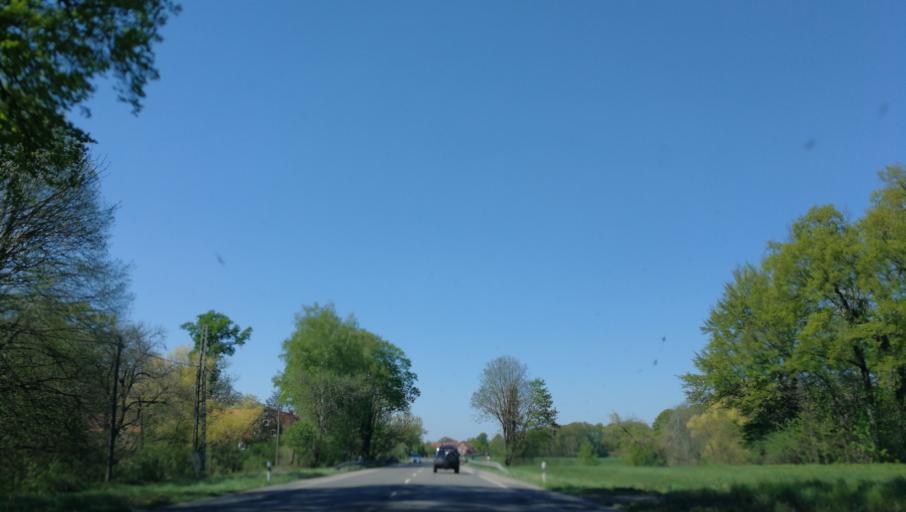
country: DE
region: North Rhine-Westphalia
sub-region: Regierungsbezirk Munster
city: Wettringen
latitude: 52.1853
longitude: 7.3336
